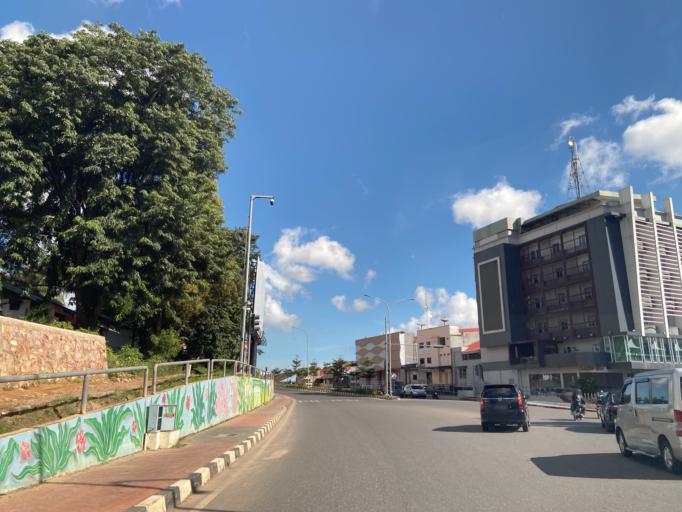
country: SG
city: Singapore
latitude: 1.1465
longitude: 104.0167
